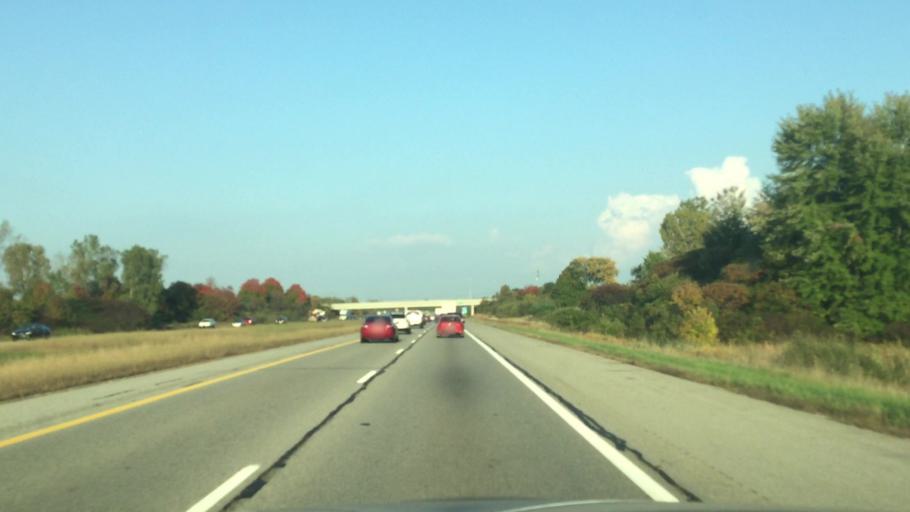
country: US
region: Michigan
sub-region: Wayne County
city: Plymouth
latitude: 42.3657
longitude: -83.5536
